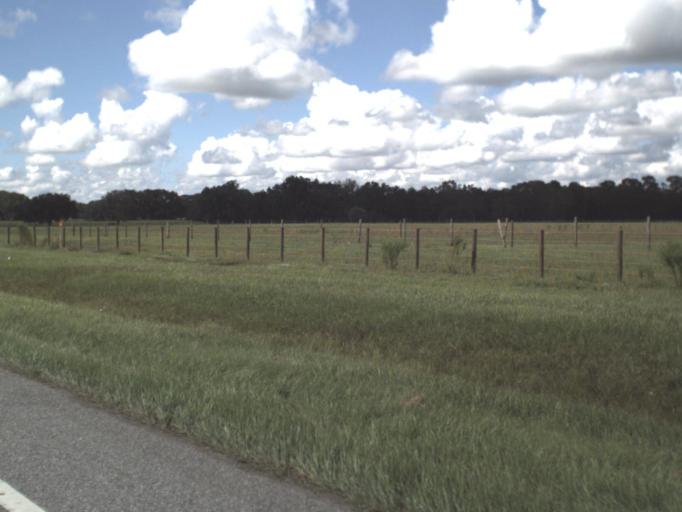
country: US
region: Florida
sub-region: Sarasota County
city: Lake Sarasota
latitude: 27.3389
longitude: -82.1444
